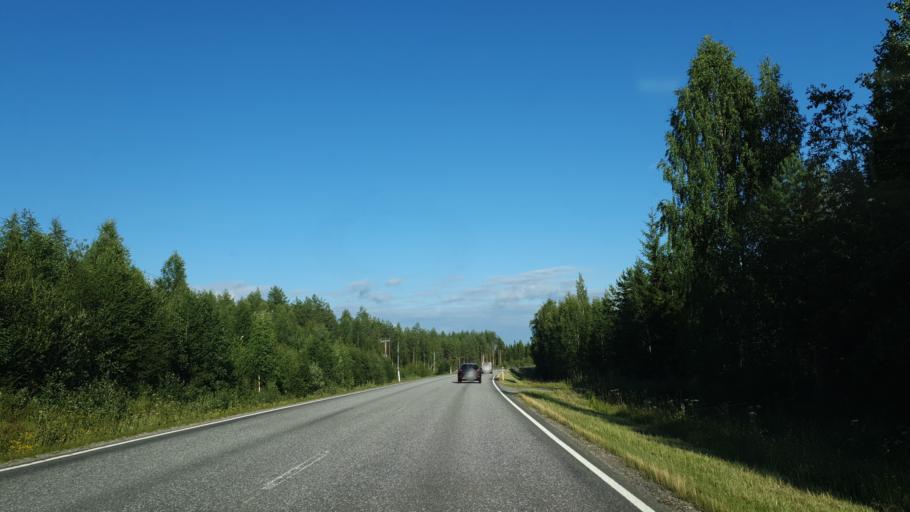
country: FI
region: North Karelia
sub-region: Joensuu
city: Outokumpu
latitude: 62.5319
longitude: 28.9734
